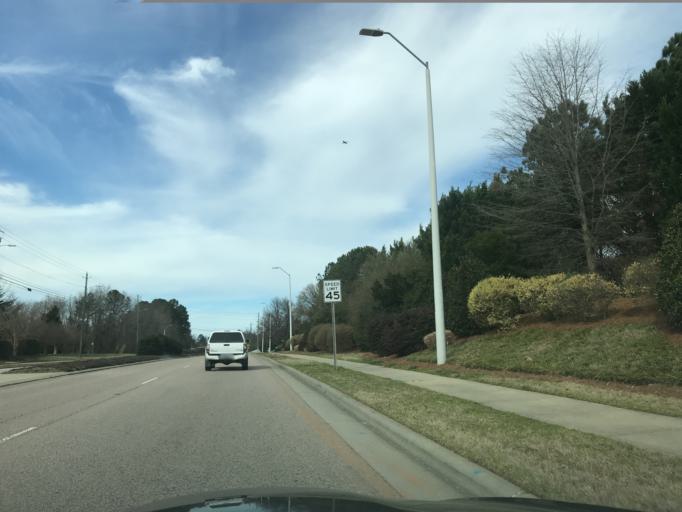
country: US
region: North Carolina
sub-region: Wake County
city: Morrisville
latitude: 35.7999
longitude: -78.8486
